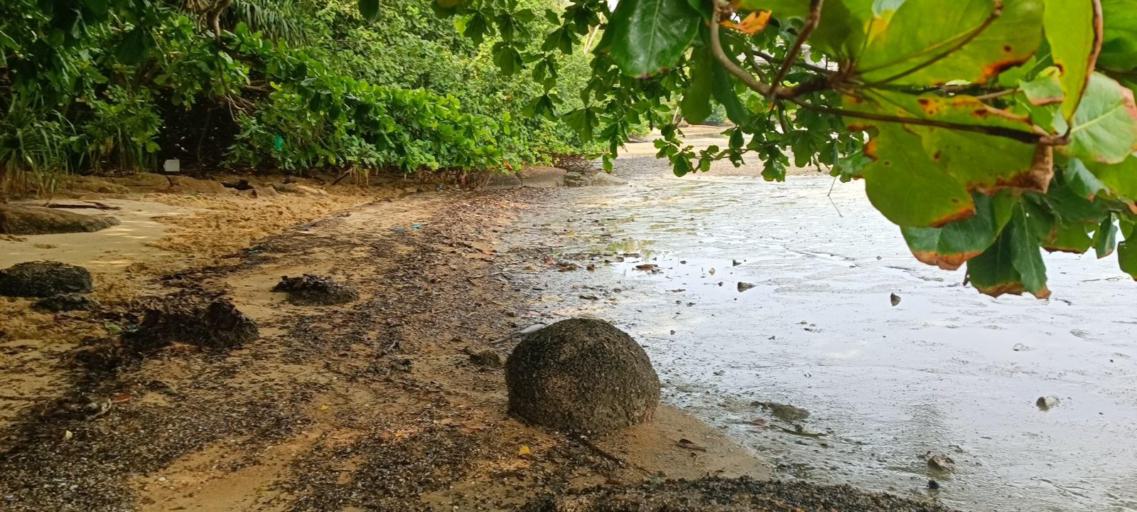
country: MY
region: Penang
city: Juru
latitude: 5.2681
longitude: 100.4092
